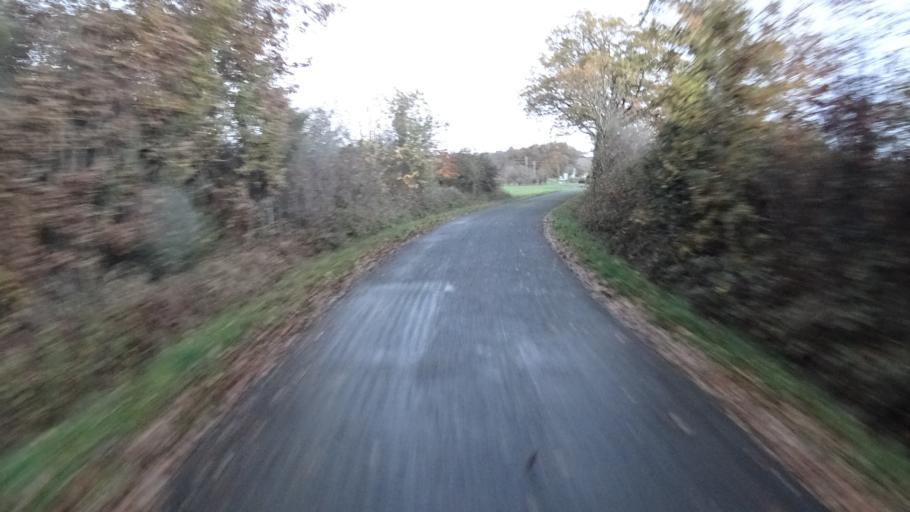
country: FR
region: Pays de la Loire
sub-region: Departement de la Loire-Atlantique
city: Avessac
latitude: 47.6631
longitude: -1.9960
